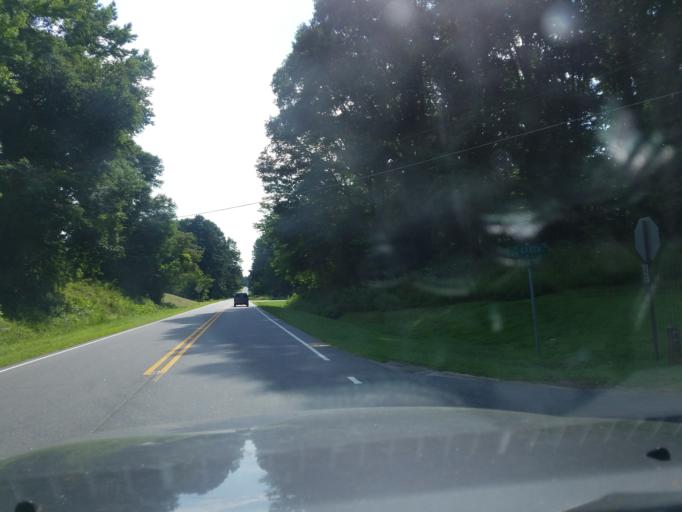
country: US
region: North Carolina
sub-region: Vance County
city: South Henderson
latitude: 36.3294
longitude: -78.4805
